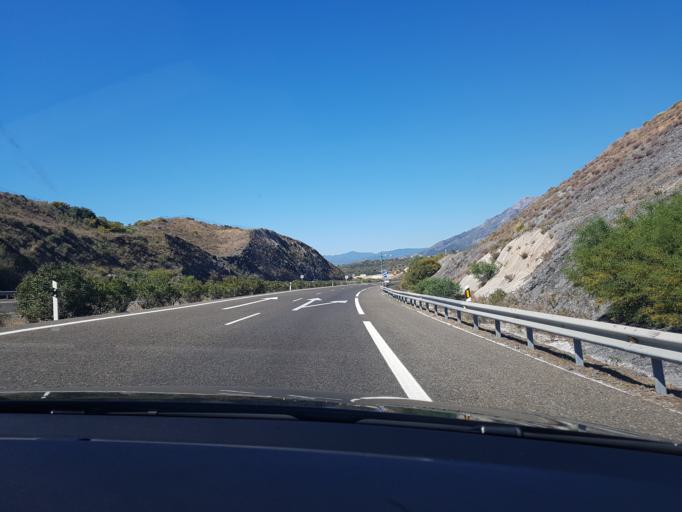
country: ES
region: Andalusia
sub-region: Provincia de Malaga
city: Ojen
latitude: 36.5150
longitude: -4.8205
